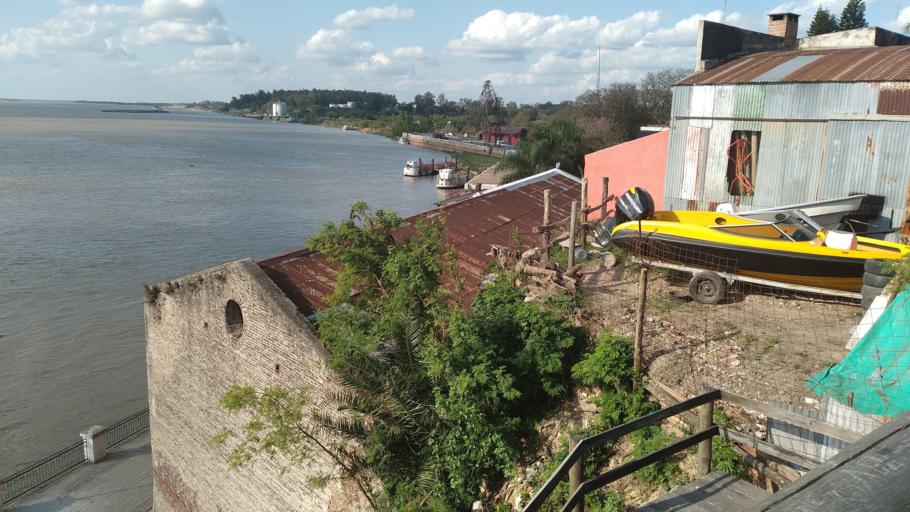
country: AR
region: Entre Rios
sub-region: Departamento de La Paz
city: La Paz
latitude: -30.7354
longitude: -59.6428
